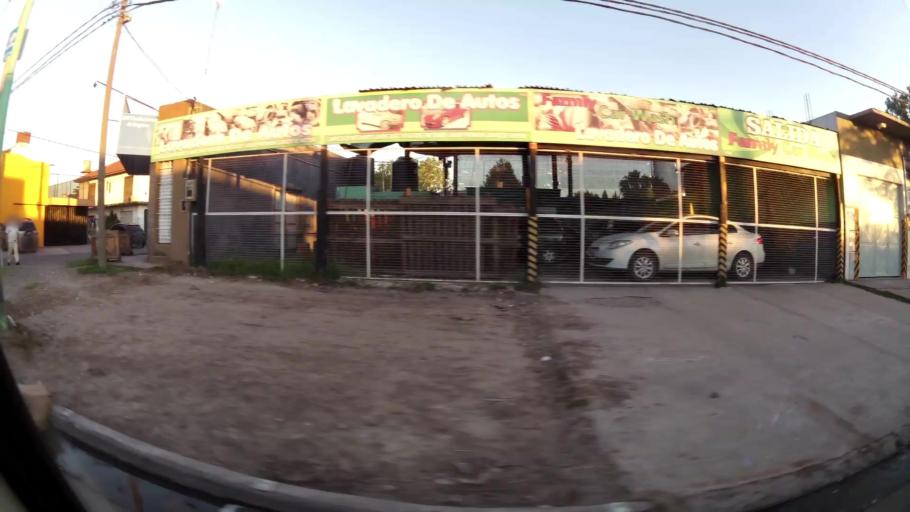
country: AR
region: Buenos Aires
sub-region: Partido de Quilmes
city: Quilmes
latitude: -34.8129
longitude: -58.1897
